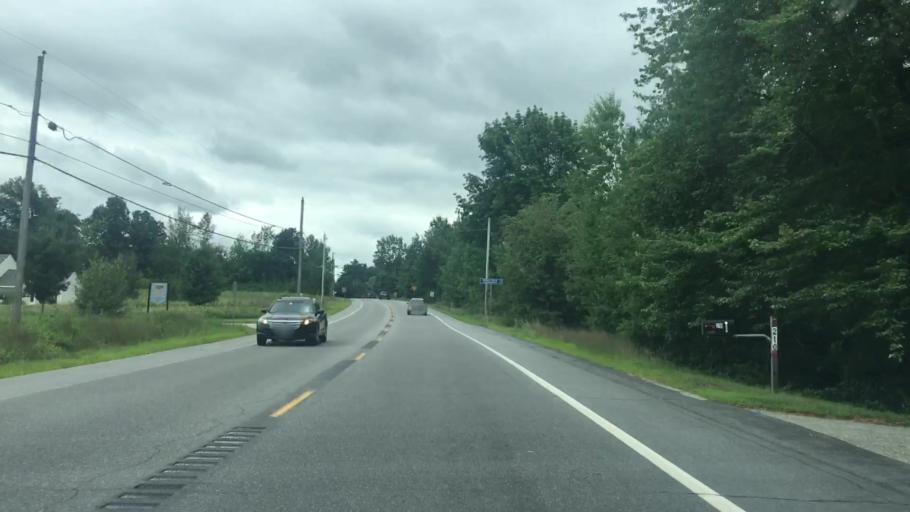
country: US
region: Maine
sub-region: York County
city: Alfred
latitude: 43.4916
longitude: -70.7199
